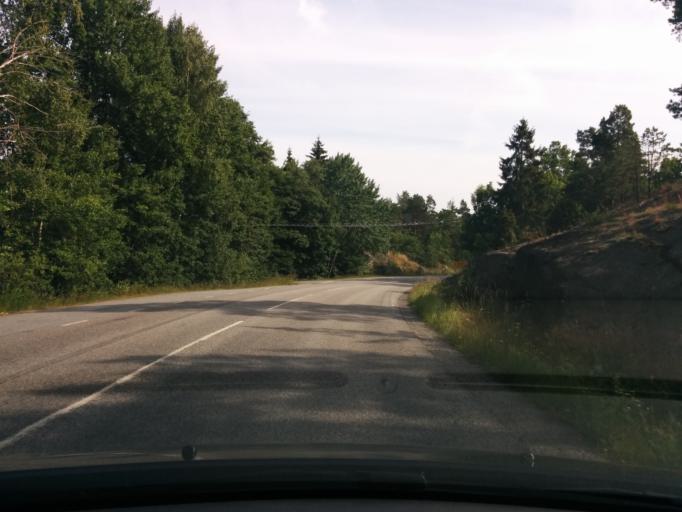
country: SE
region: Stockholm
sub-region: Varmdo Kommun
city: Holo
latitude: 59.3286
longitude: 18.7229
